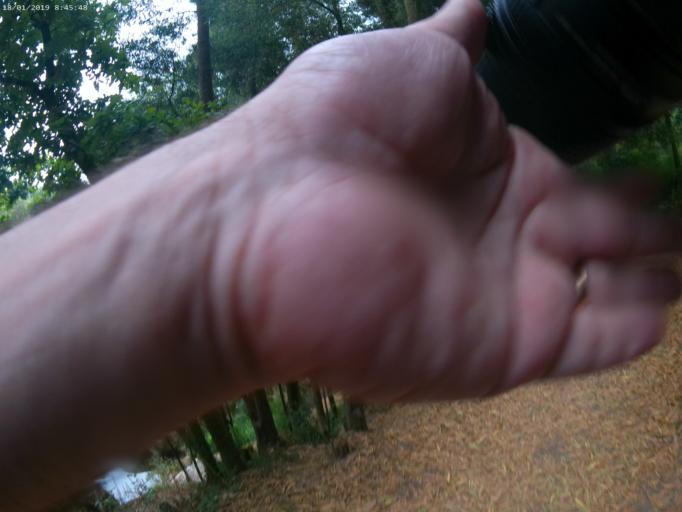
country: PT
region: Viana do Castelo
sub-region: Ponte da Barca
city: Ponte da Barca
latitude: 41.8099
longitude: -8.4301
